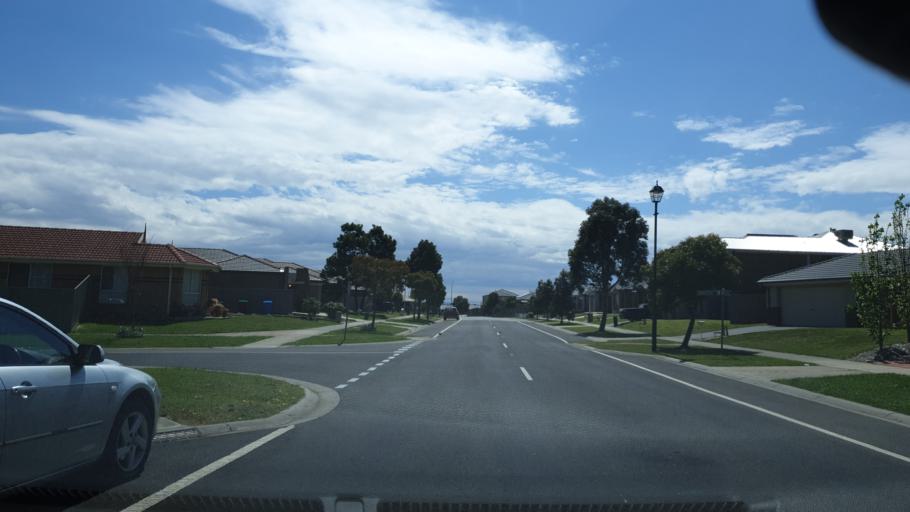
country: AU
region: Victoria
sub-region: Casey
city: Cranbourne East
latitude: -38.1028
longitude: 145.3074
